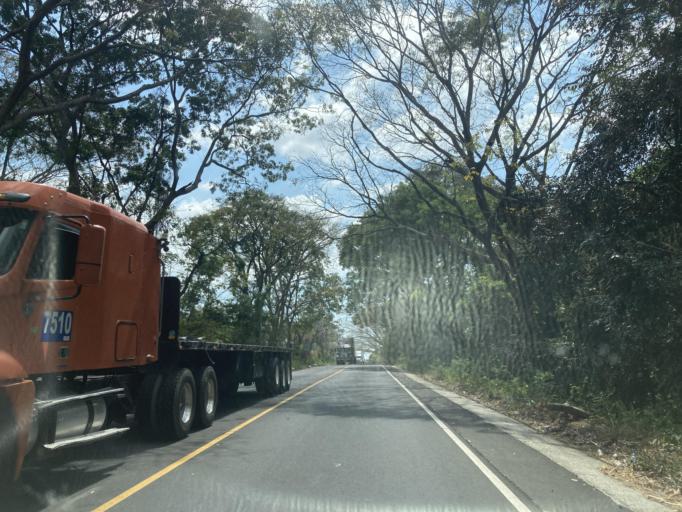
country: GT
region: Santa Rosa
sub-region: Municipio de Taxisco
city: Taxisco
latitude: 14.0744
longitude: -90.4761
